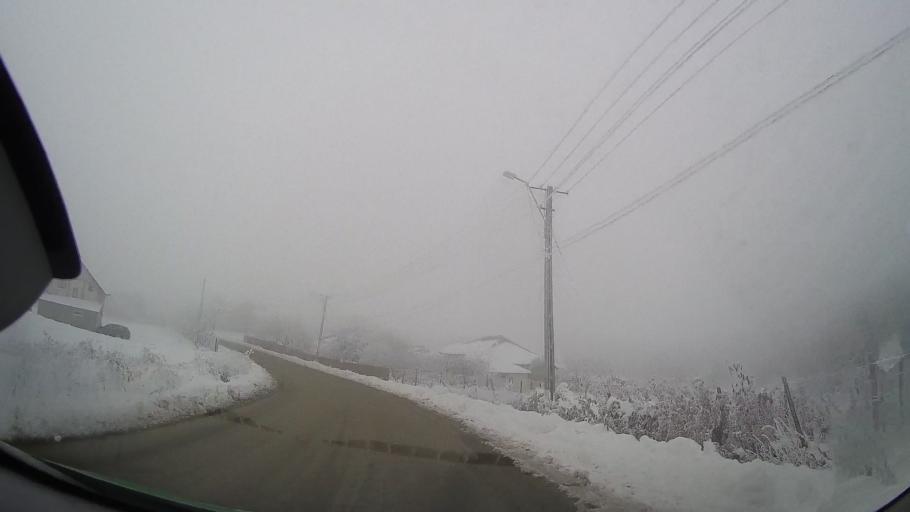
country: RO
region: Iasi
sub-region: Comuna Tansa
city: Suhulet
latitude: 46.9005
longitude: 27.2488
